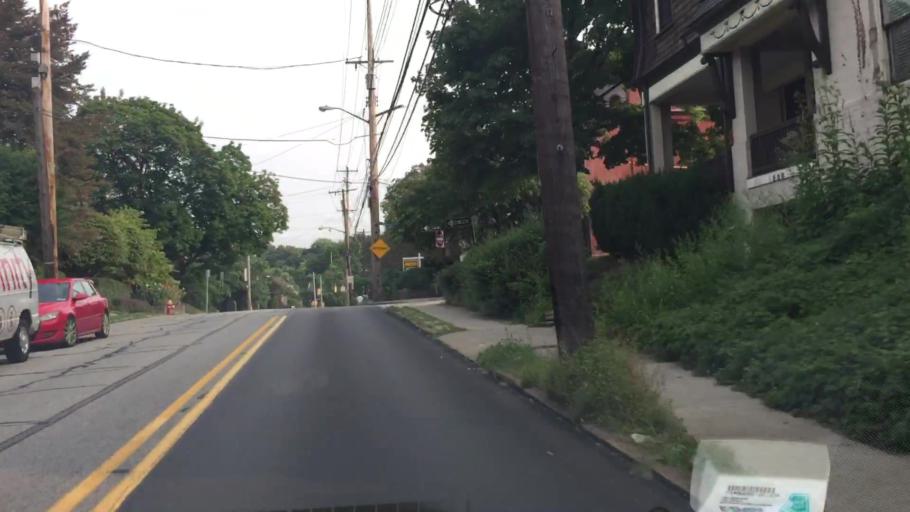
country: US
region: Pennsylvania
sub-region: Allegheny County
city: Bloomfield
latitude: 40.4534
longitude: -79.9441
